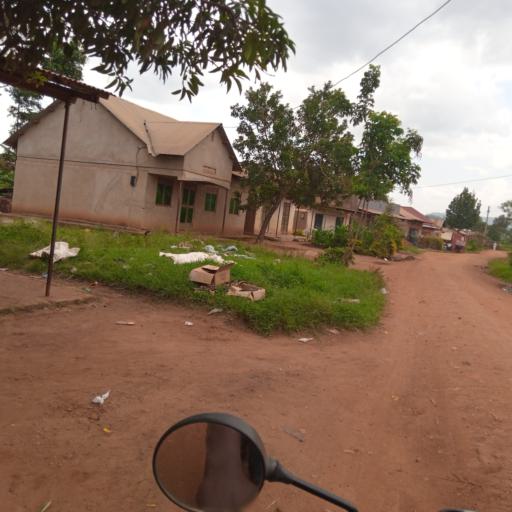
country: UG
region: Eastern Region
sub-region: Mbale District
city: Mbale
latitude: 1.1148
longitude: 34.1734
